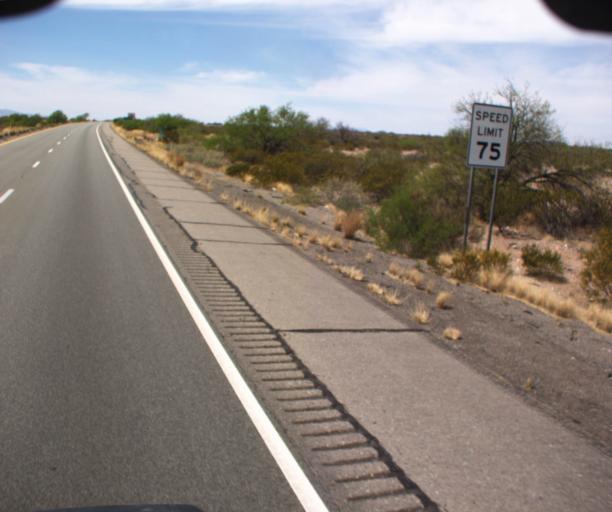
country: US
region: New Mexico
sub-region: Hidalgo County
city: Lordsburg
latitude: 32.2398
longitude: -109.1002
